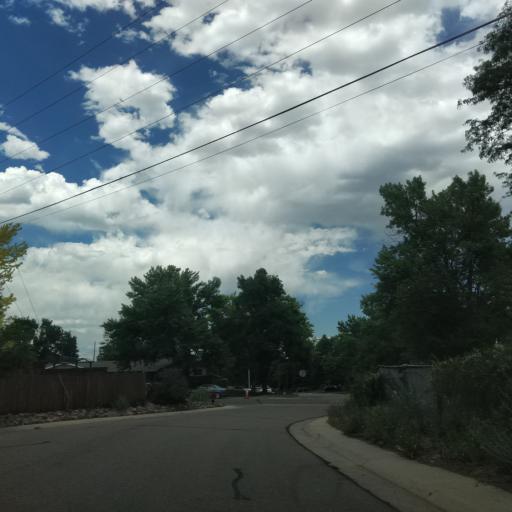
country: US
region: Colorado
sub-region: Jefferson County
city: Lakewood
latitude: 39.6856
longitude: -105.0873
